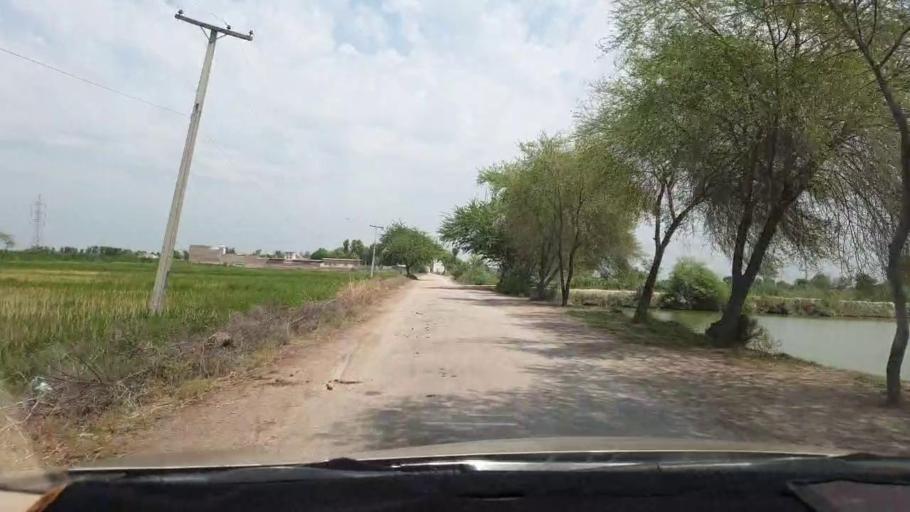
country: PK
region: Sindh
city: Naudero
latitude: 27.7228
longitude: 68.3347
